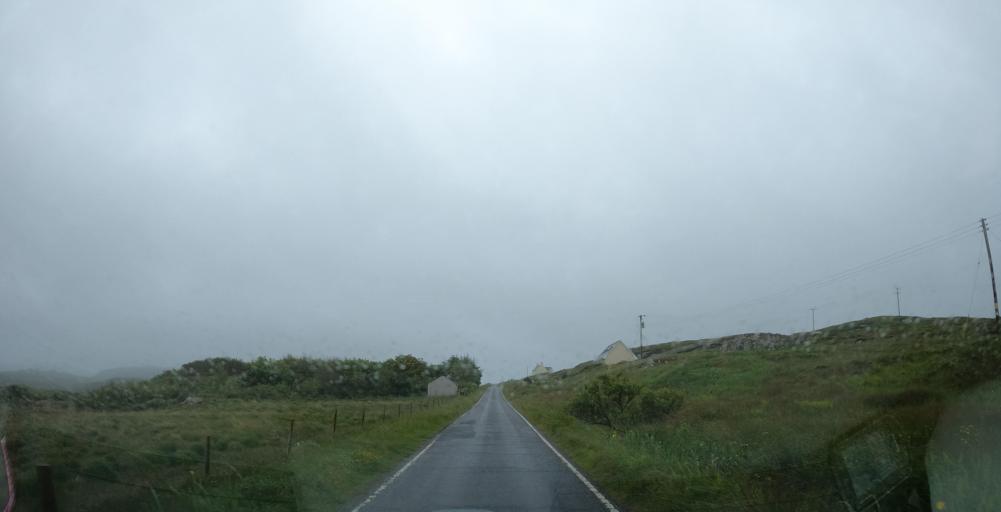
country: GB
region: Scotland
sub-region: Eilean Siar
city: Barra
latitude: 56.9887
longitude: -7.4156
